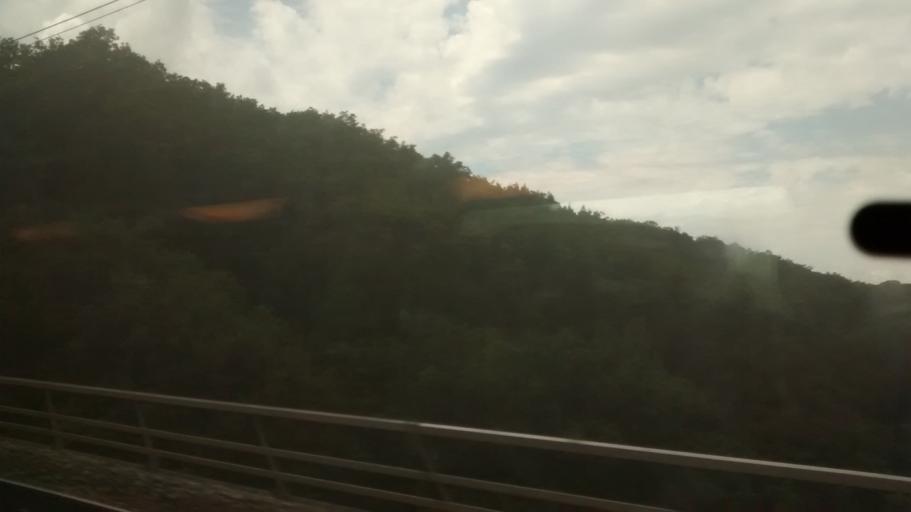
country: FR
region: Bourgogne
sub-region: Departement de la Cote-d'Or
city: Saulieu
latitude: 47.2910
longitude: 4.2721
